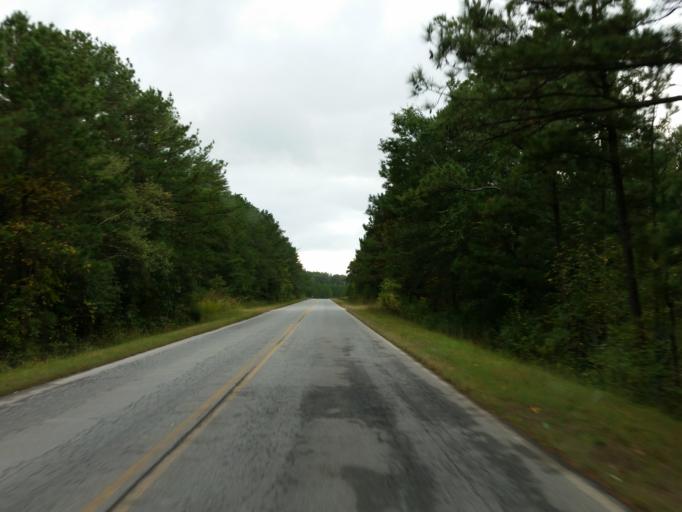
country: US
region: Georgia
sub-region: Bartow County
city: Cartersville
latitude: 34.1150
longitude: -84.8448
